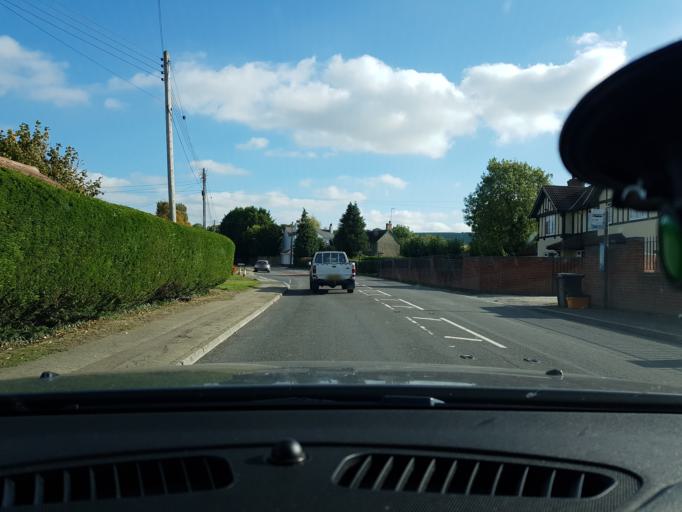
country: GB
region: England
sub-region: Borough of Swindon
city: Wanborough
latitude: 51.5344
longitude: -1.7112
